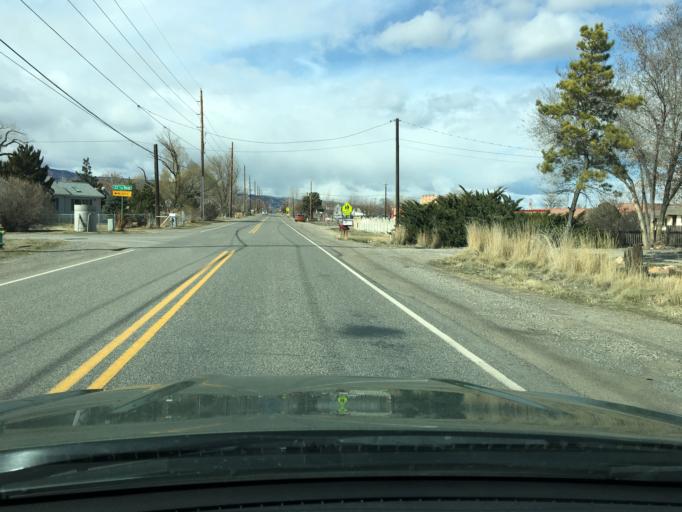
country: US
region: Colorado
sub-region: Mesa County
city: Redlands
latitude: 39.1209
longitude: -108.6136
